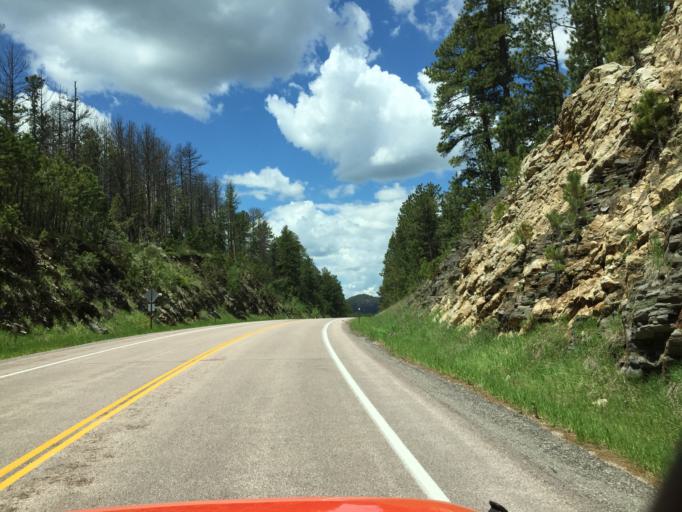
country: US
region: South Dakota
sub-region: Custer County
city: Custer
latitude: 43.8946
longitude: -103.5708
